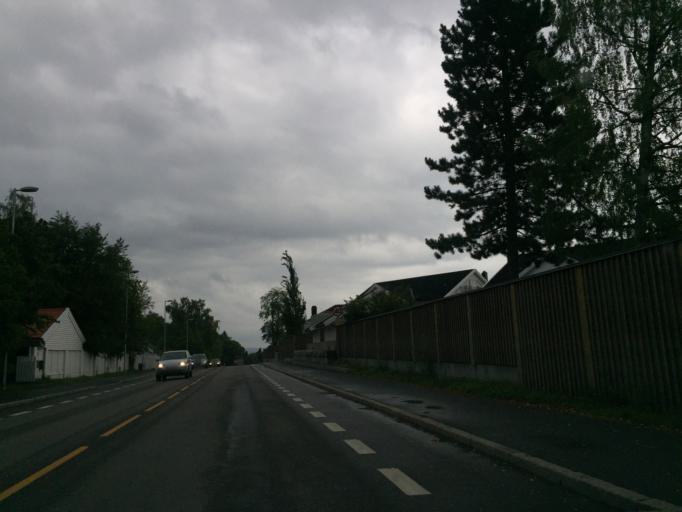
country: NO
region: Oslo
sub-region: Oslo
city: Sjolyststranda
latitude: 59.9463
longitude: 10.6776
